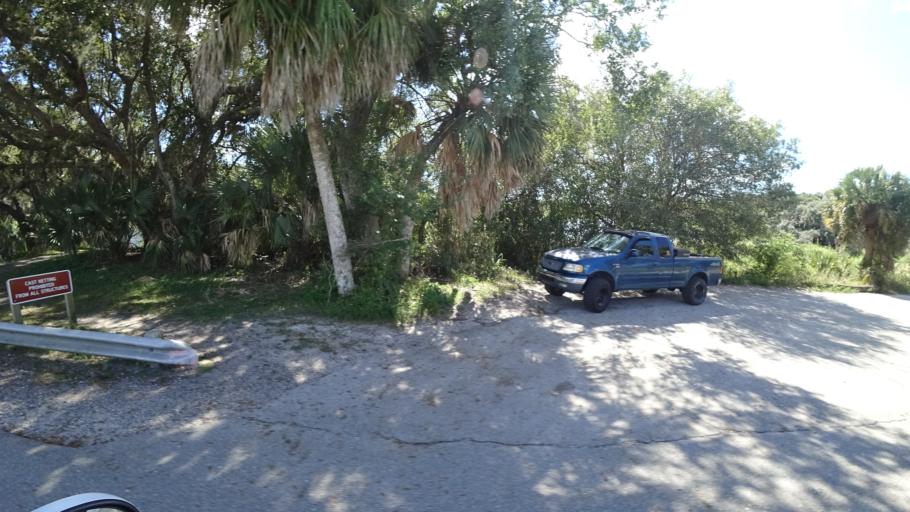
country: US
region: Florida
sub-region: Sarasota County
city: Lake Sarasota
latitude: 27.2457
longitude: -82.3075
